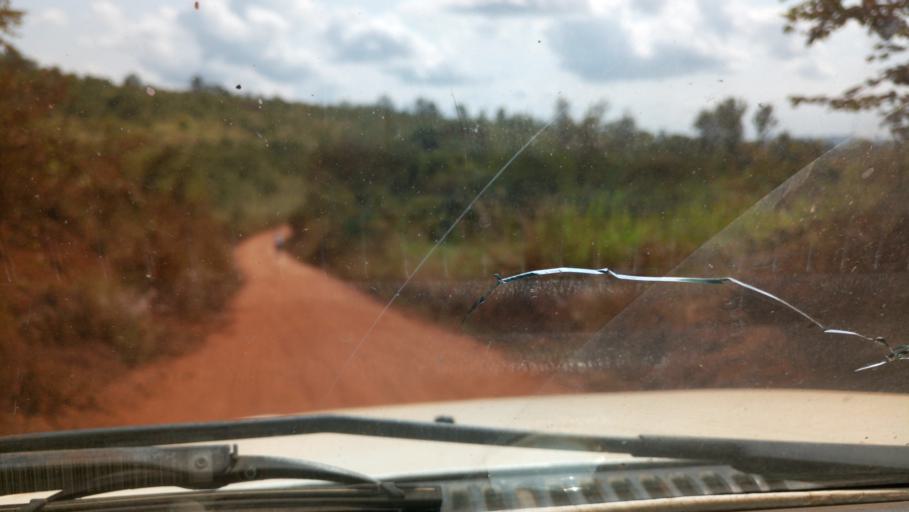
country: KE
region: Murang'a District
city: Murang'a
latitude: -0.7432
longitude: 37.1758
